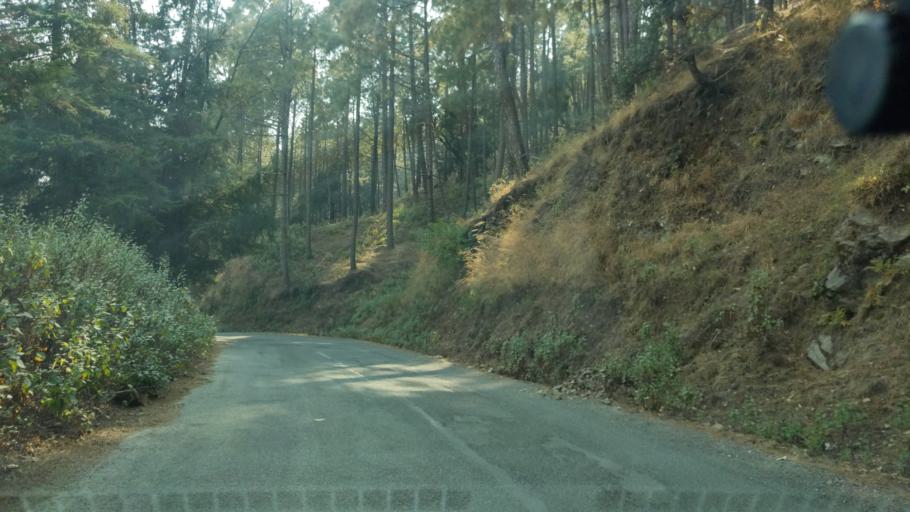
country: IN
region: Uttarakhand
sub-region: Naini Tal
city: Bhowali
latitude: 29.3949
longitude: 79.5391
